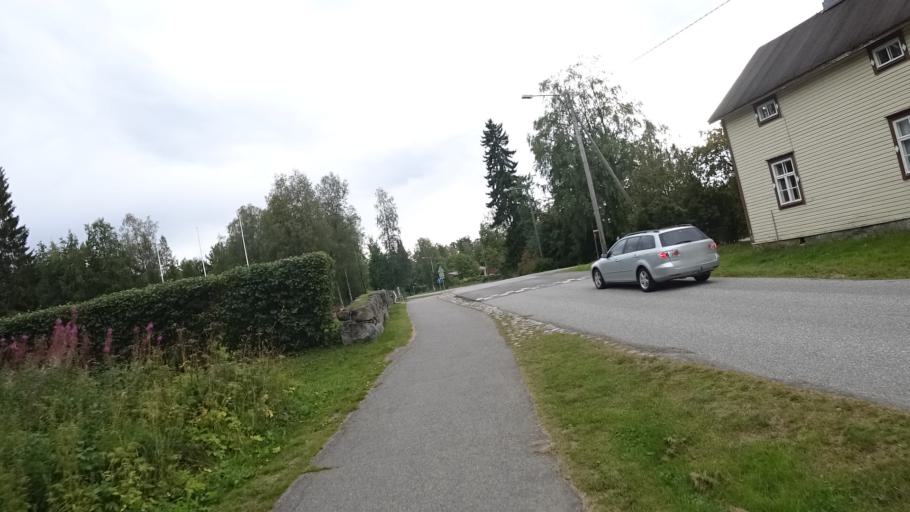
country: FI
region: North Karelia
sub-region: Joensuu
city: Ilomantsi
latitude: 62.6780
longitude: 30.9171
